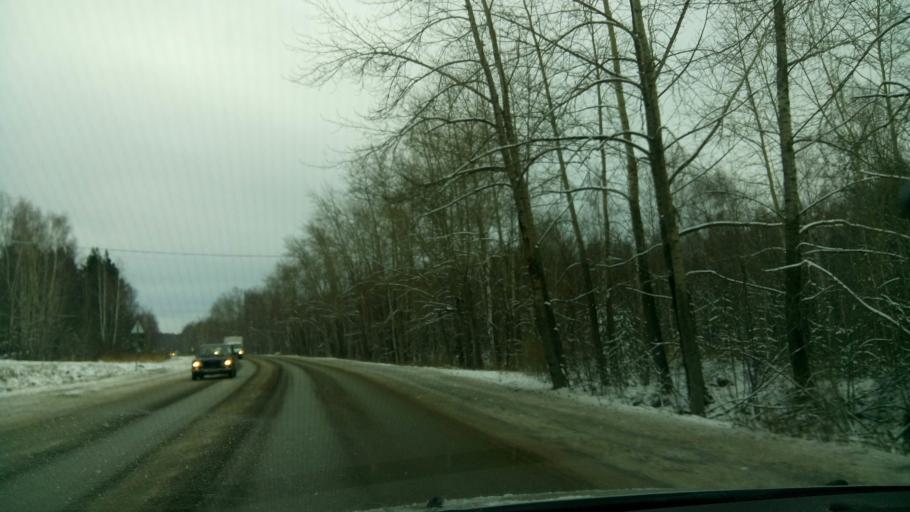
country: RU
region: Sverdlovsk
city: Polevskoy
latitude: 56.4688
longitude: 60.2277
